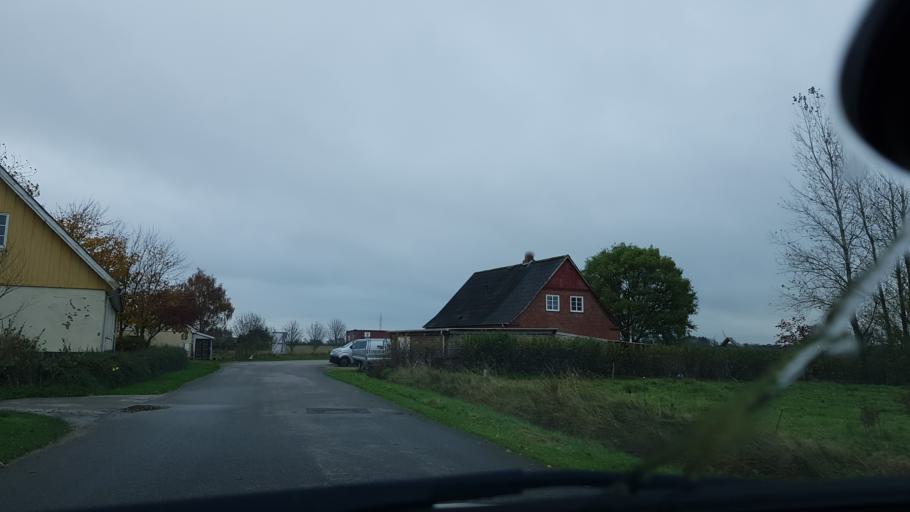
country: DK
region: South Denmark
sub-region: Tonder Kommune
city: Sherrebek
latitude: 55.2128
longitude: 8.8086
